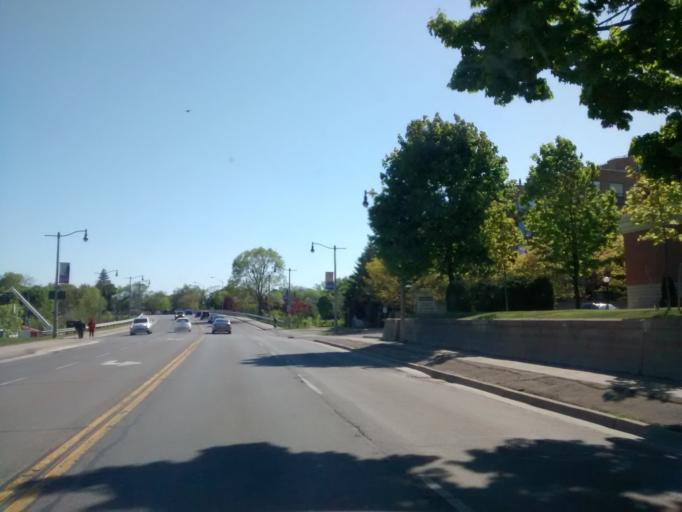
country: CA
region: Ontario
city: Oakville
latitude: 43.3934
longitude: -79.7128
